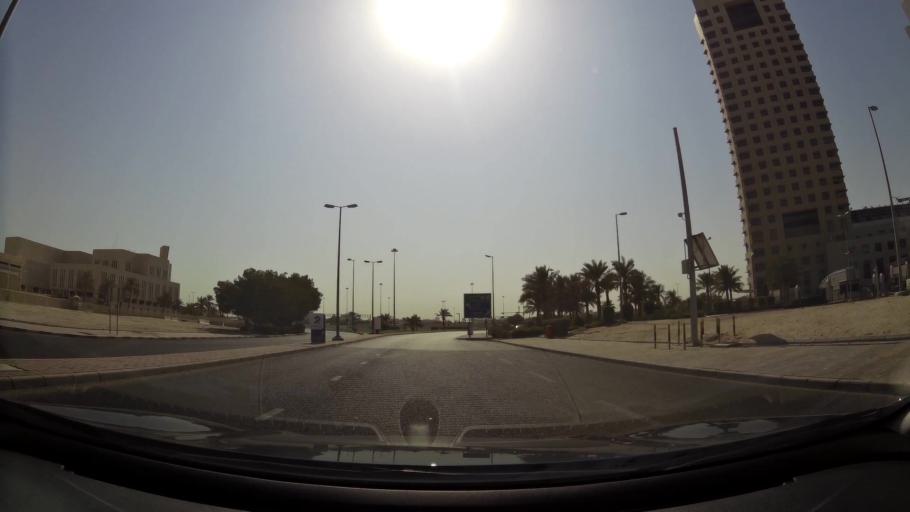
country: KW
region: Al Asimah
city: Kuwait City
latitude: 29.3645
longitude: 47.9841
